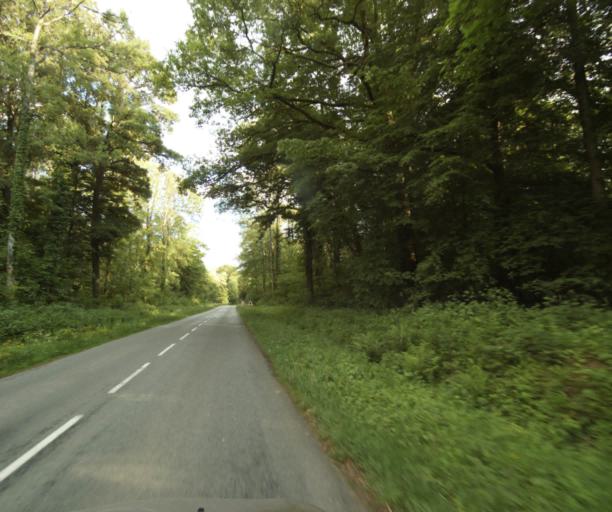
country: FR
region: Champagne-Ardenne
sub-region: Departement des Ardennes
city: Warcq
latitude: 49.8168
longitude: 4.7007
